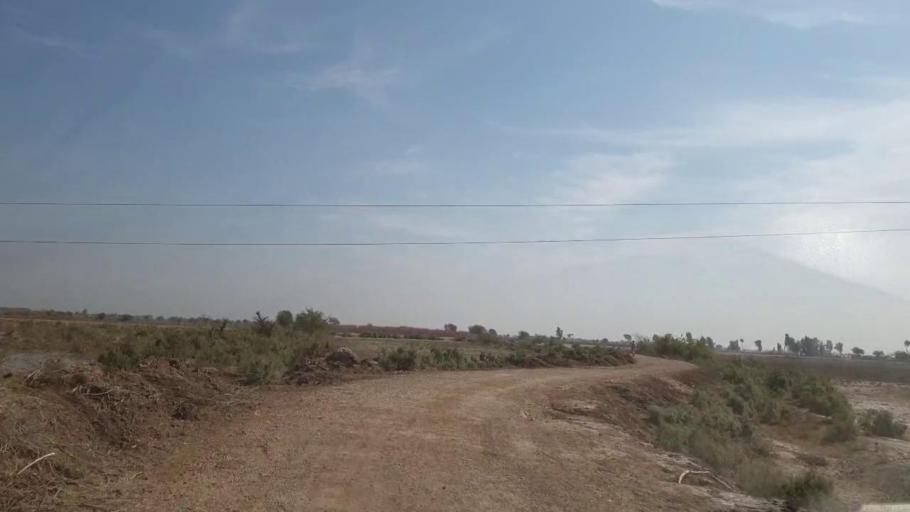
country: PK
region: Sindh
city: Mirpur Khas
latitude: 25.5761
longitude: 69.1856
